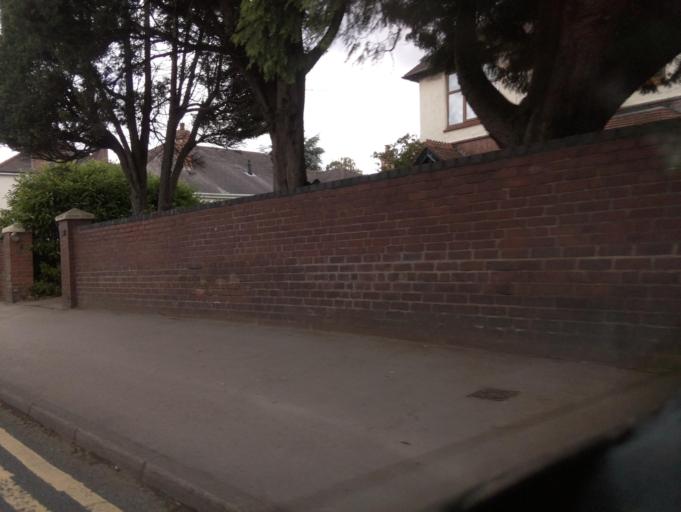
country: GB
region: England
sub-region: Worcestershire
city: Kidderminster
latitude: 52.3873
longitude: -2.2335
